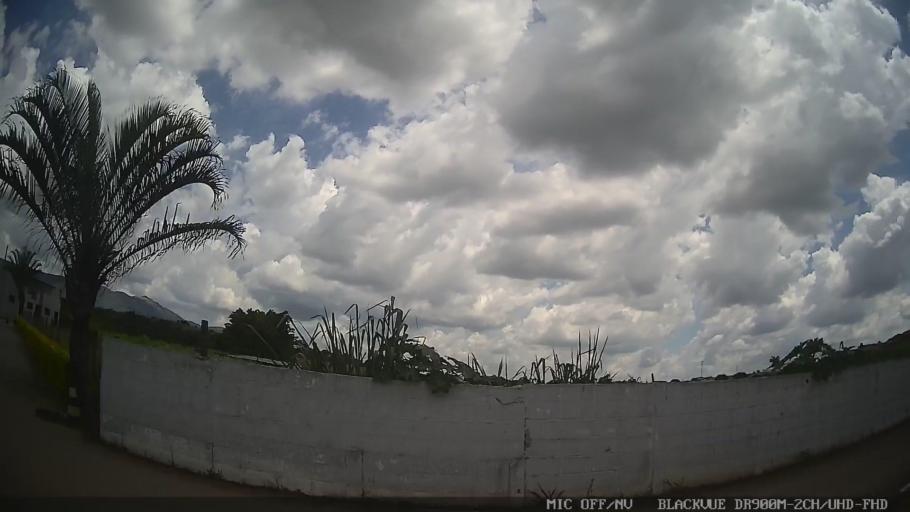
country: BR
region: Sao Paulo
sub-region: Atibaia
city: Atibaia
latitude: -23.1172
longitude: -46.5791
